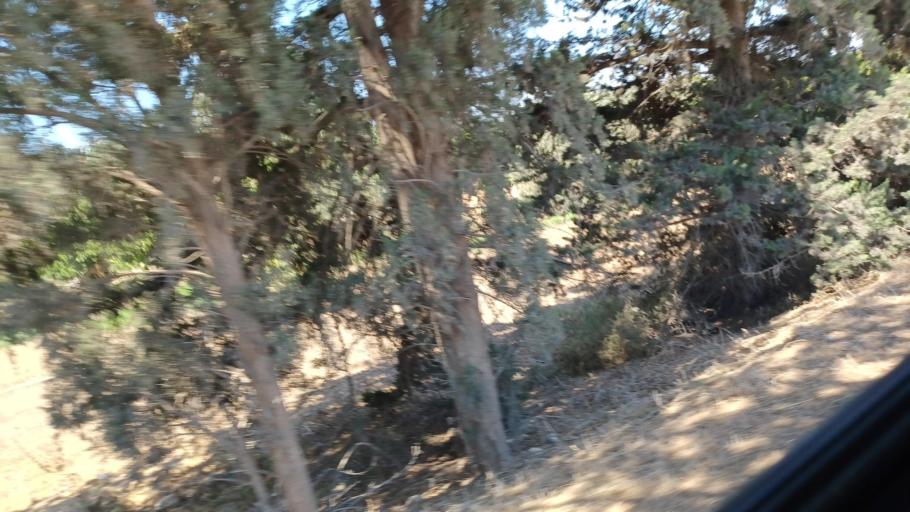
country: CY
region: Ammochostos
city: Acheritou
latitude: 35.0843
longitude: 33.8866
